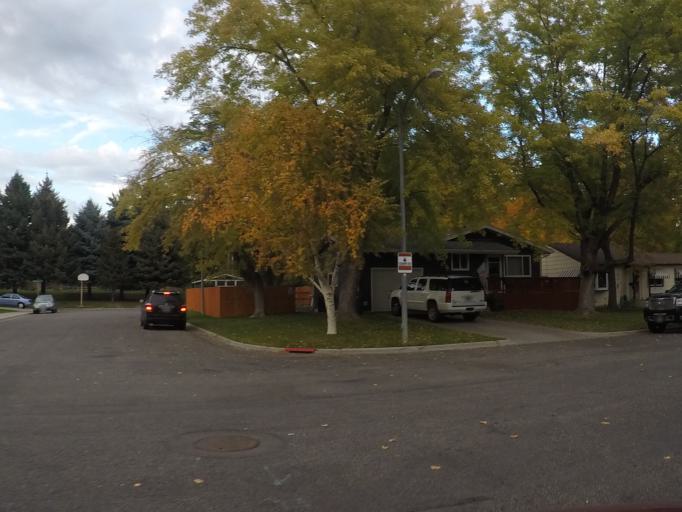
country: US
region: Montana
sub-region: Yellowstone County
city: Billings
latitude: 45.7921
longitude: -108.5512
